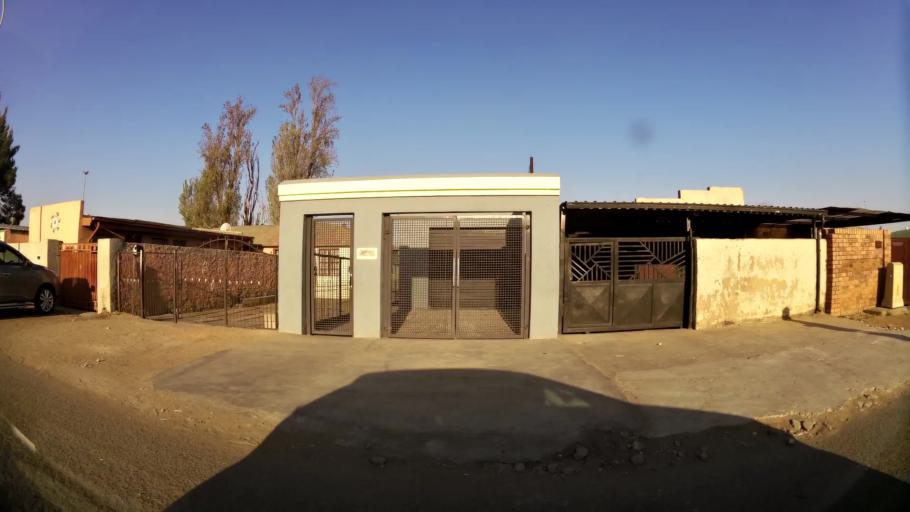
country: ZA
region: Gauteng
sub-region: City of Johannesburg Metropolitan Municipality
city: Soweto
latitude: -26.2555
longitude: 27.8802
